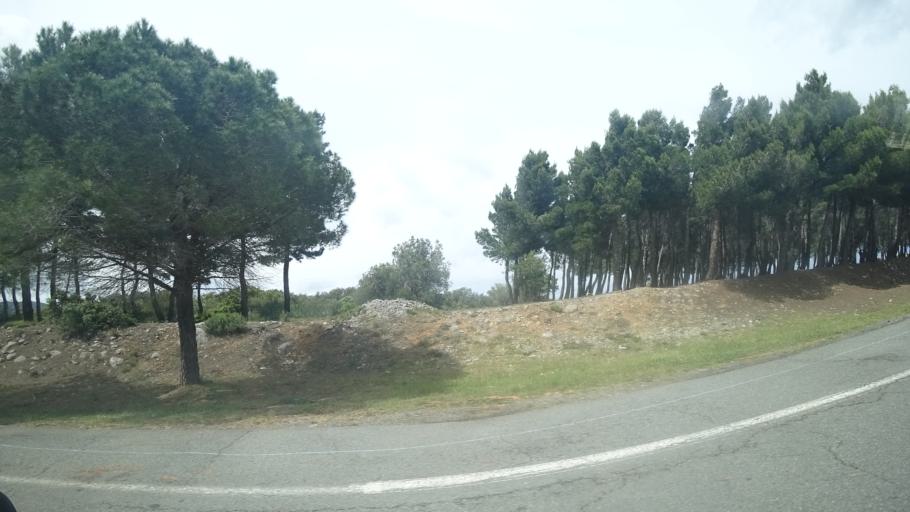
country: FR
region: Languedoc-Roussillon
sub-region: Departement de l'Aude
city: Leucate
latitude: 42.9392
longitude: 2.9725
